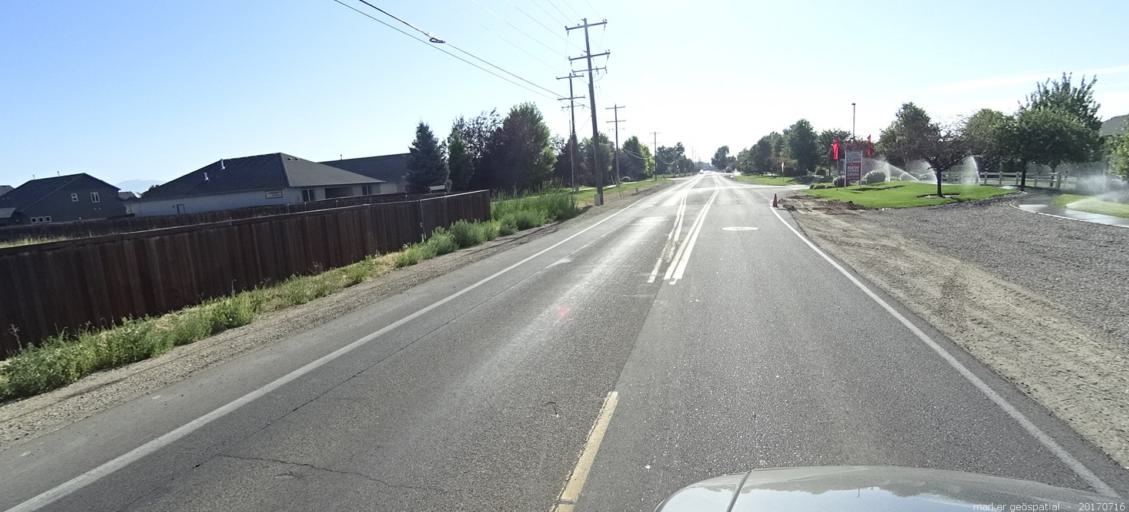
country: US
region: Idaho
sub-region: Ada County
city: Garden City
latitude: 43.5465
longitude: -116.3097
